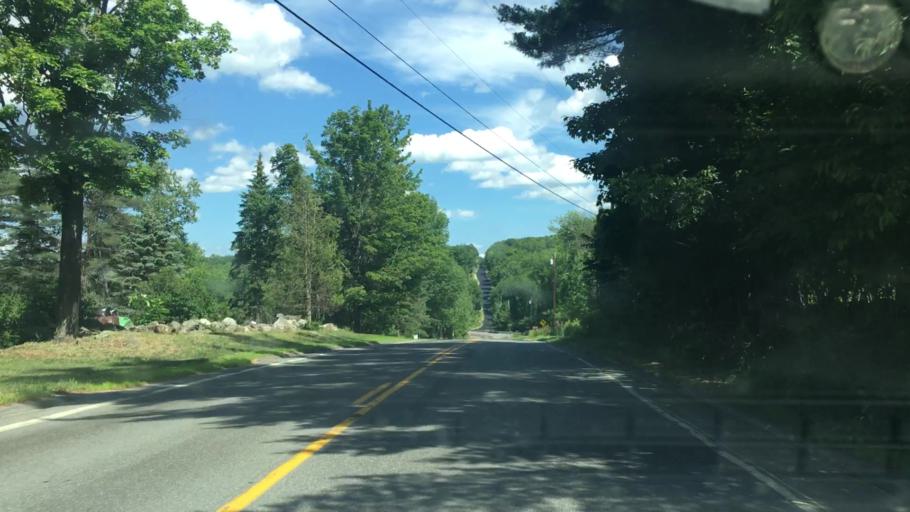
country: US
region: Maine
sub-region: Franklin County
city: Wilton
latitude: 44.5761
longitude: -70.1686
